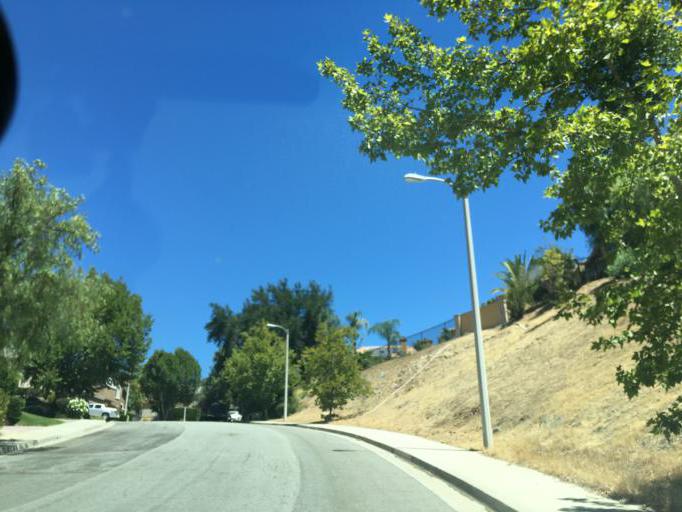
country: US
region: California
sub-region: Los Angeles County
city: Agoura Hills
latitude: 34.1153
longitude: -118.7779
